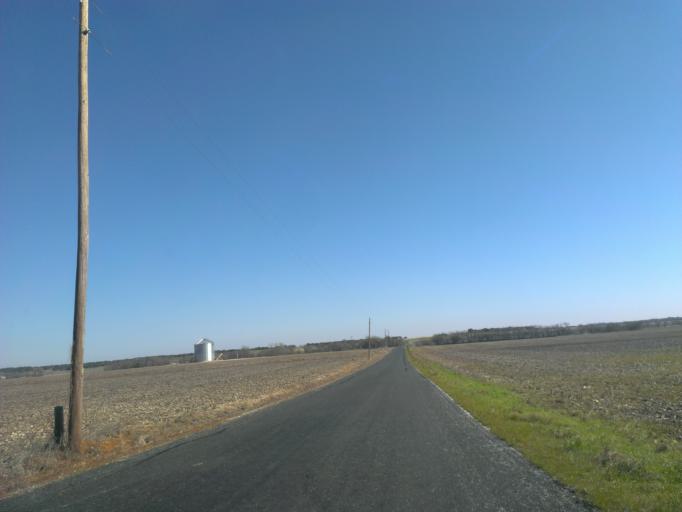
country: US
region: Texas
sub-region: Williamson County
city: Georgetown
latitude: 30.6566
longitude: -97.5682
